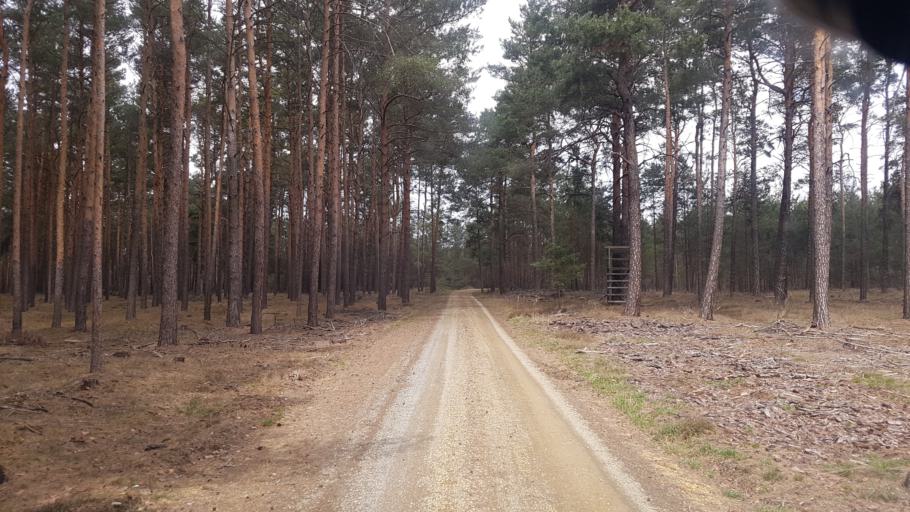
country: DE
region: Brandenburg
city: Schonborn
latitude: 51.6548
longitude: 13.4960
